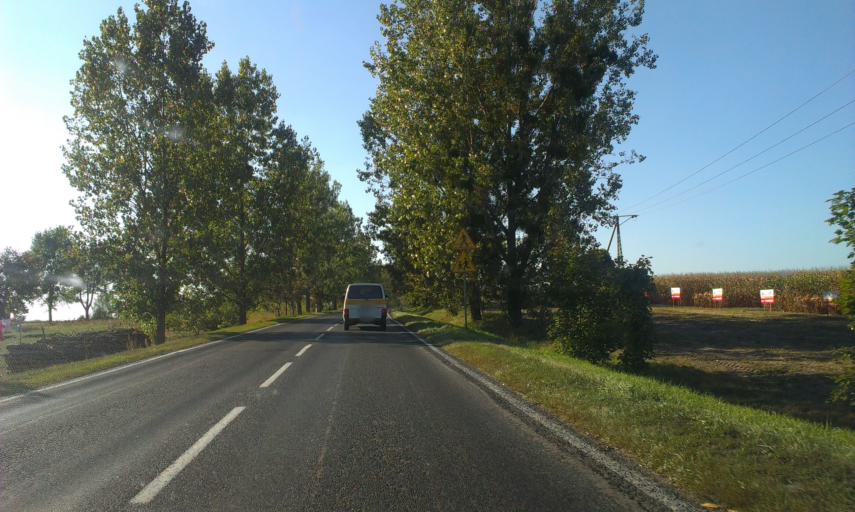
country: PL
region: Kujawsko-Pomorskie
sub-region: Powiat swiecki
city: Drzycim
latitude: 53.4189
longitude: 18.3485
